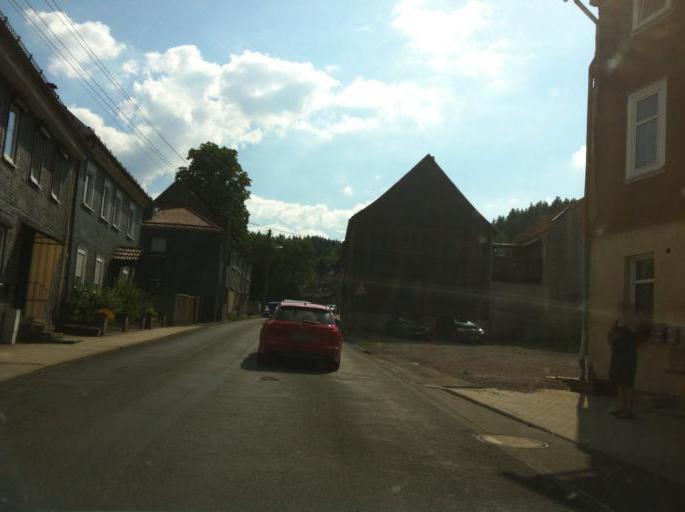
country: DE
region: Thuringia
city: Mohrenbach
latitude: 50.6232
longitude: 10.9946
